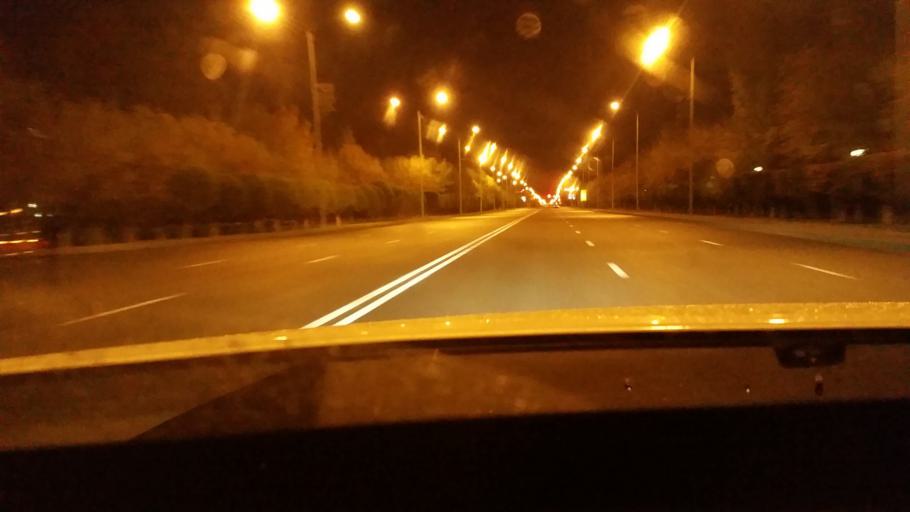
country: KZ
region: Astana Qalasy
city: Astana
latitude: 51.1537
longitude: 71.4880
